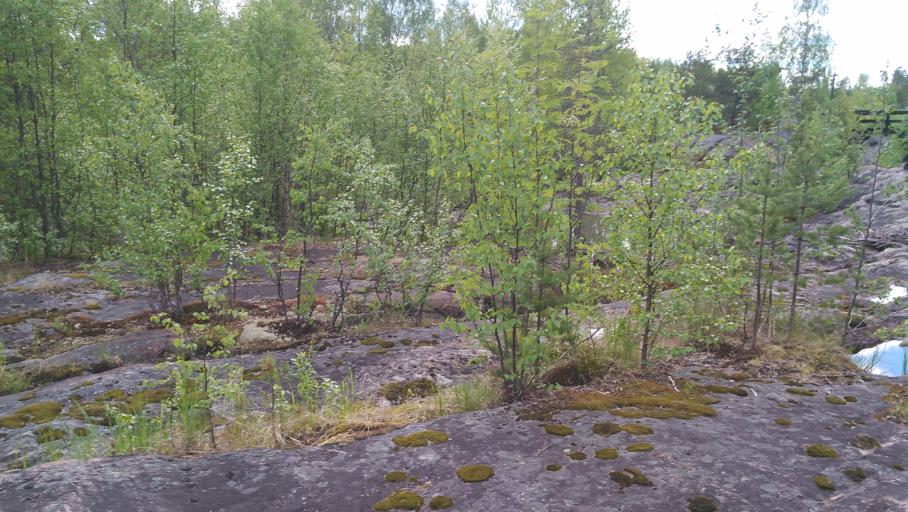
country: SE
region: Vaesterbotten
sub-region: Umea Kommun
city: Roback
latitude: 63.8796
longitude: 20.0256
